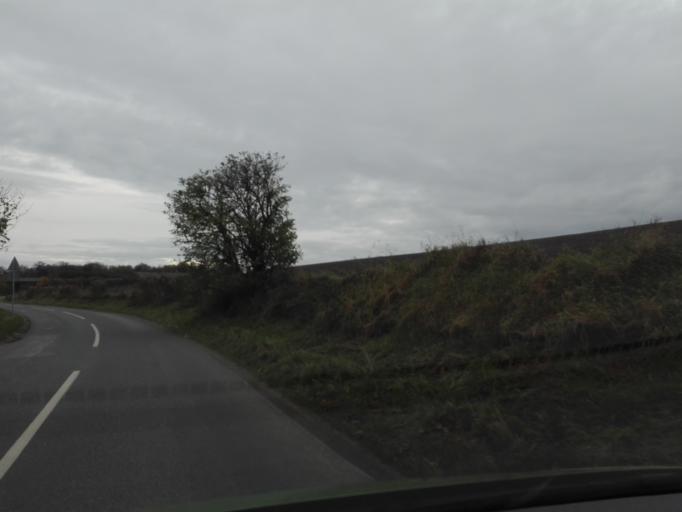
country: DK
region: Central Jutland
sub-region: Arhus Kommune
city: Solbjerg
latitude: 56.0636
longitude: 10.0870
